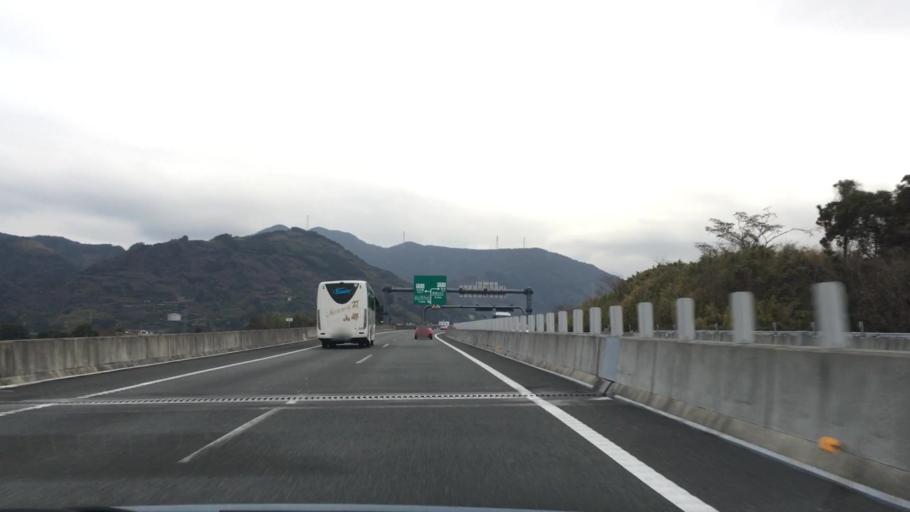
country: JP
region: Shizuoka
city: Shizuoka-shi
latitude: 35.0514
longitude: 138.4858
